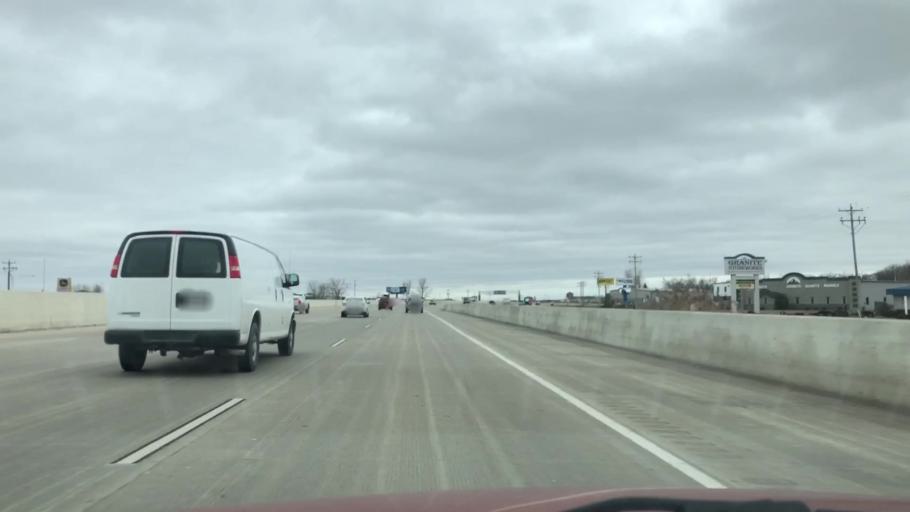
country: US
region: Wisconsin
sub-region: Brown County
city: De Pere
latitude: 44.4410
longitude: -88.0980
